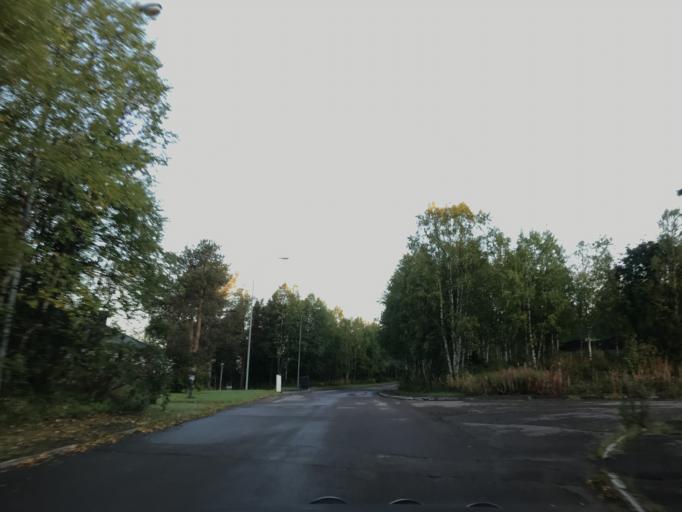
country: SE
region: Norrbotten
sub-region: Gallivare Kommun
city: Malmberget
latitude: 67.6495
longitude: 21.0469
